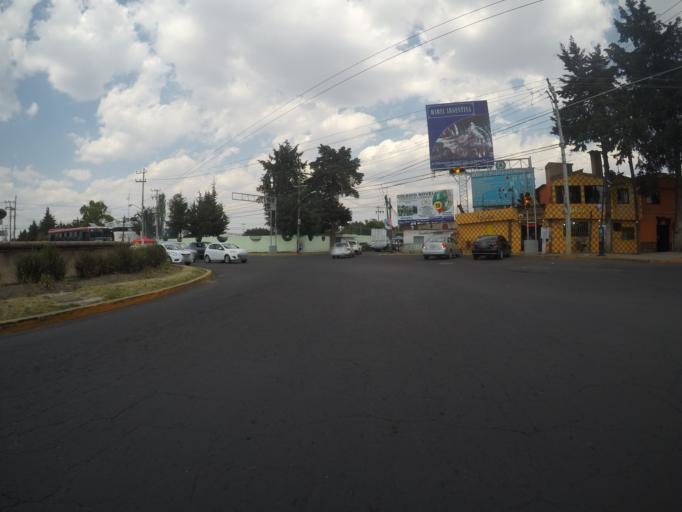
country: MX
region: Mexico
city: San Buenaventura
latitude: 19.2564
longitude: -99.6632
